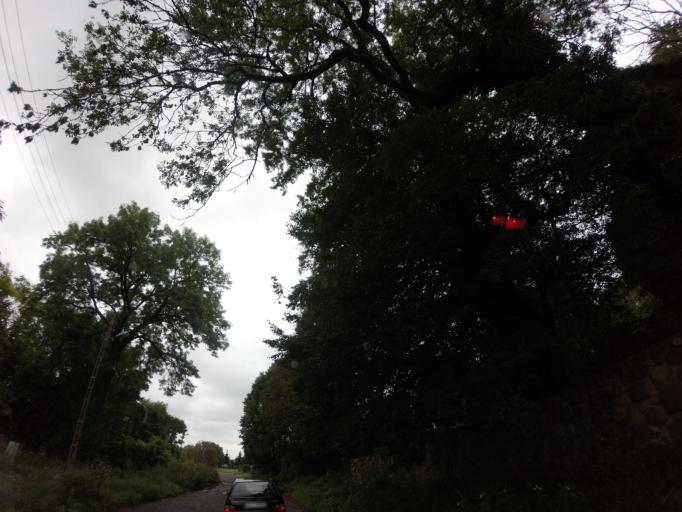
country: PL
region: West Pomeranian Voivodeship
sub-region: Powiat choszczenski
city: Choszczno
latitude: 53.1791
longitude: 15.3244
